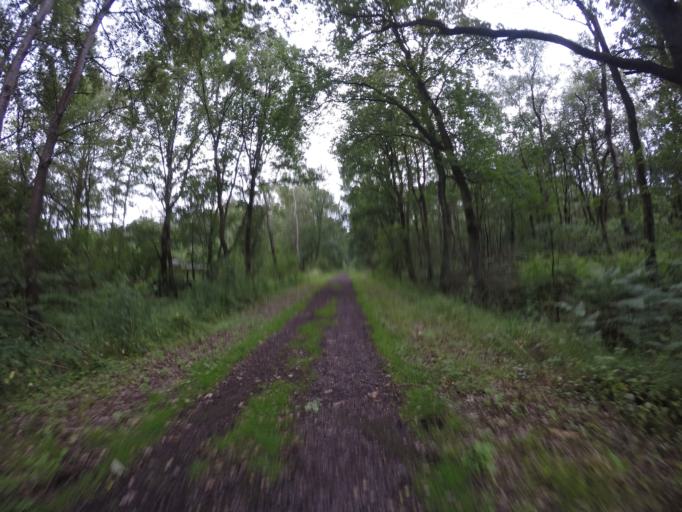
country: DE
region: North Rhine-Westphalia
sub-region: Regierungsbezirk Dusseldorf
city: Schermbeck
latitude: 51.5996
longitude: 6.8553
